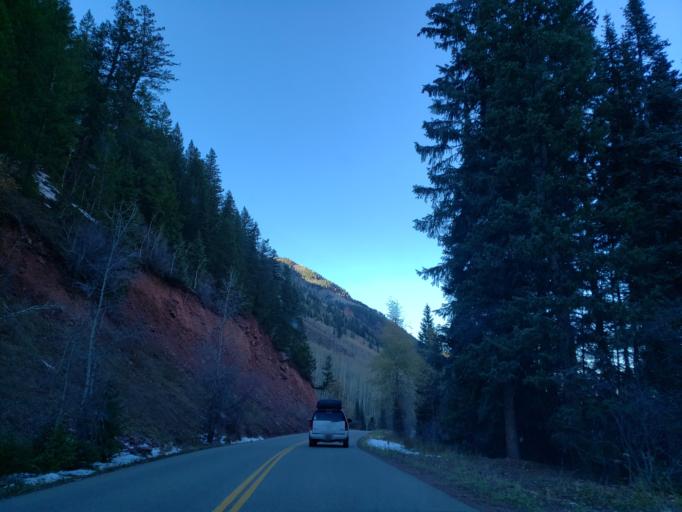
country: US
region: Colorado
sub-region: Pitkin County
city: Snowmass Village
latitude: 39.1331
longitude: -106.9018
